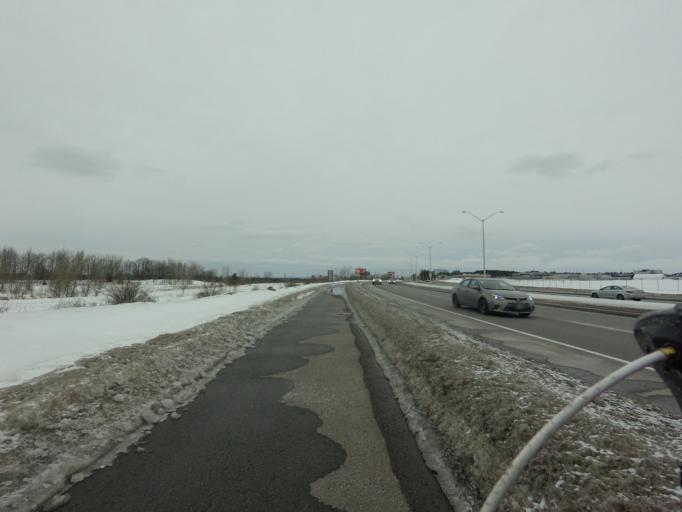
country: CA
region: Ontario
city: Ottawa
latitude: 45.3302
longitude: -75.6940
